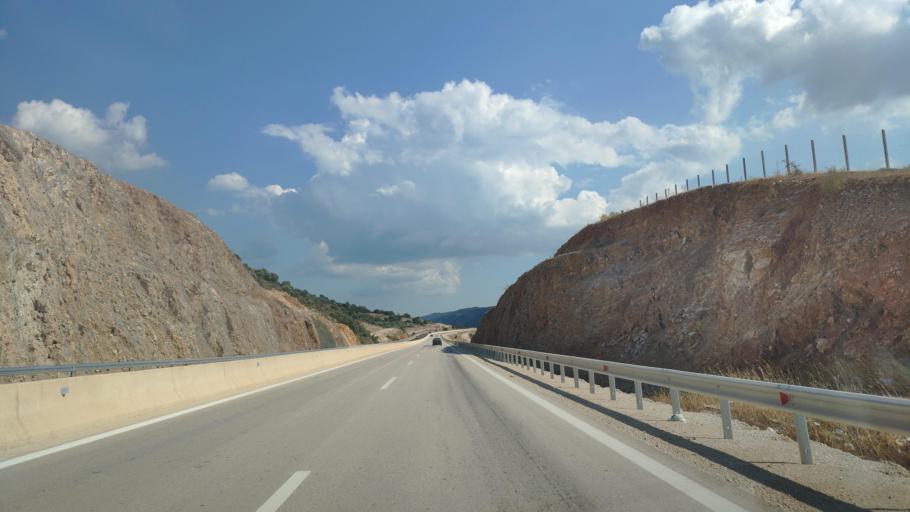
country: GR
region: West Greece
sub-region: Nomos Aitolias kai Akarnanias
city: Katouna
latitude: 38.8185
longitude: 21.1266
